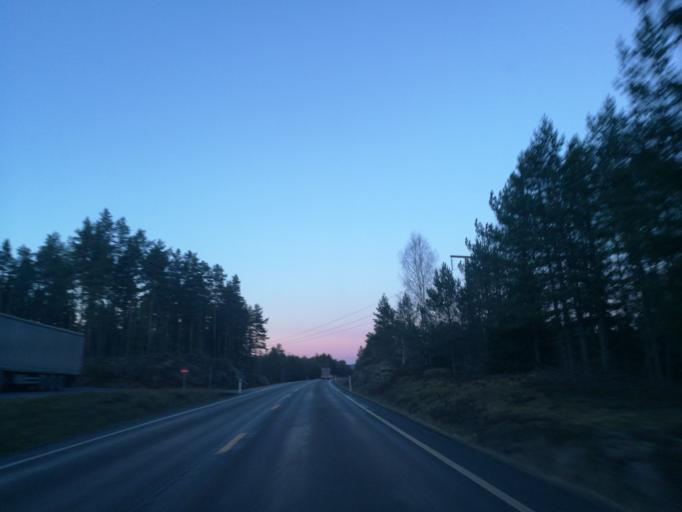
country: NO
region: Hedmark
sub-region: Eidskog
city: Skotterud
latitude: 60.0127
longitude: 12.1090
